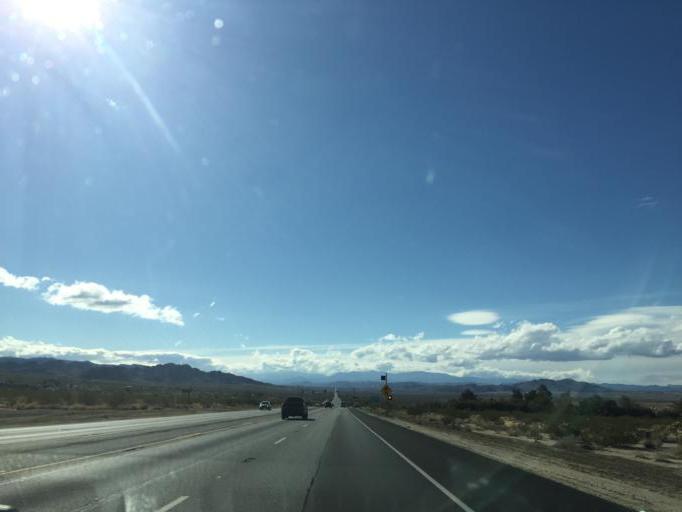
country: US
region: California
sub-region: San Bernardino County
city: Joshua Tree
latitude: 34.1352
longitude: -116.2085
